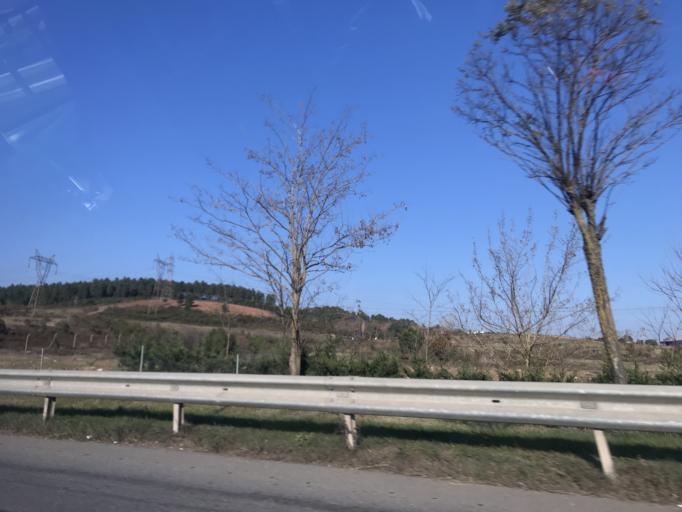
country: TR
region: Istanbul
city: Sultanbeyli
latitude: 40.9388
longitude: 29.3322
